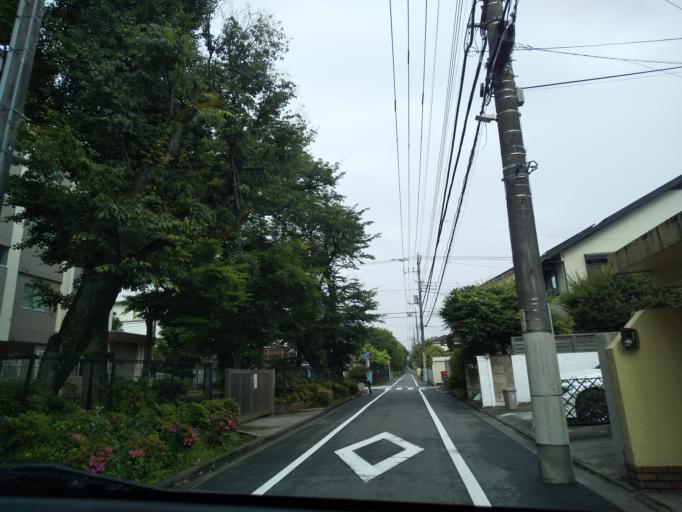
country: JP
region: Tokyo
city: Kokubunji
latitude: 35.6886
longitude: 139.4506
